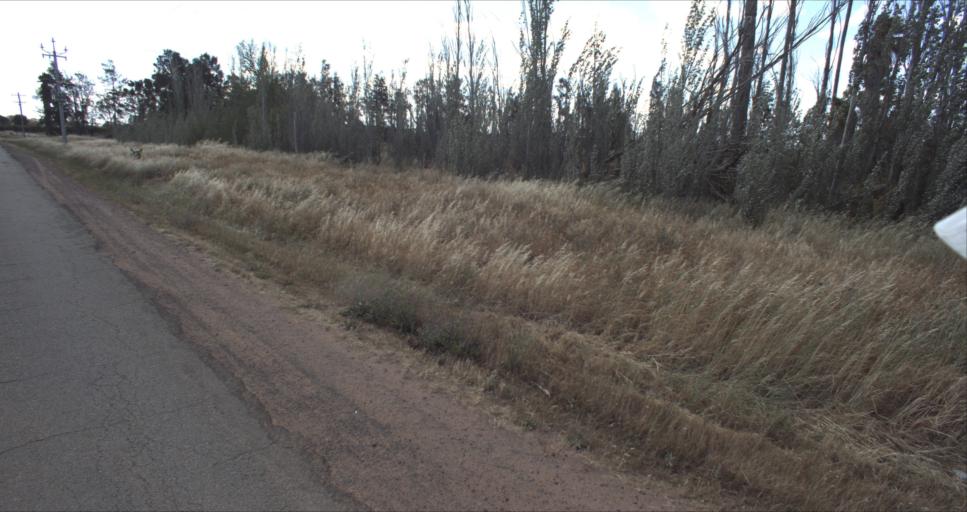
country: AU
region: New South Wales
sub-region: Leeton
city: Leeton
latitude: -34.5134
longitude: 146.2462
